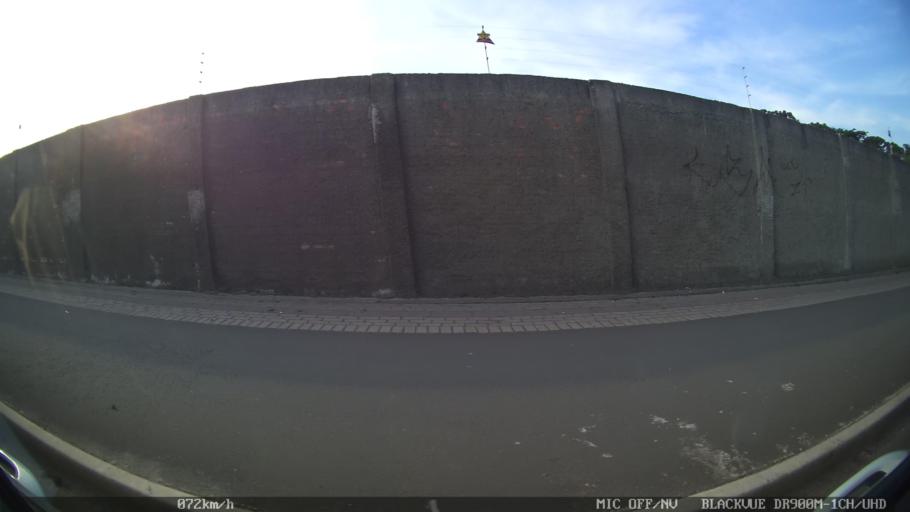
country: BR
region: Parana
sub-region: Piraquara
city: Piraquara
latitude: -25.4527
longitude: -49.1162
